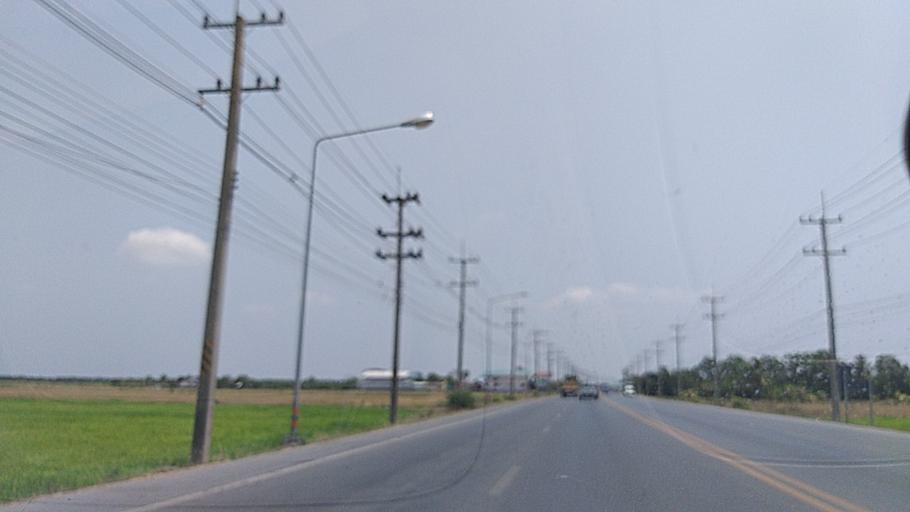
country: TH
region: Bangkok
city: Nong Chok
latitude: 13.9675
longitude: 100.9405
